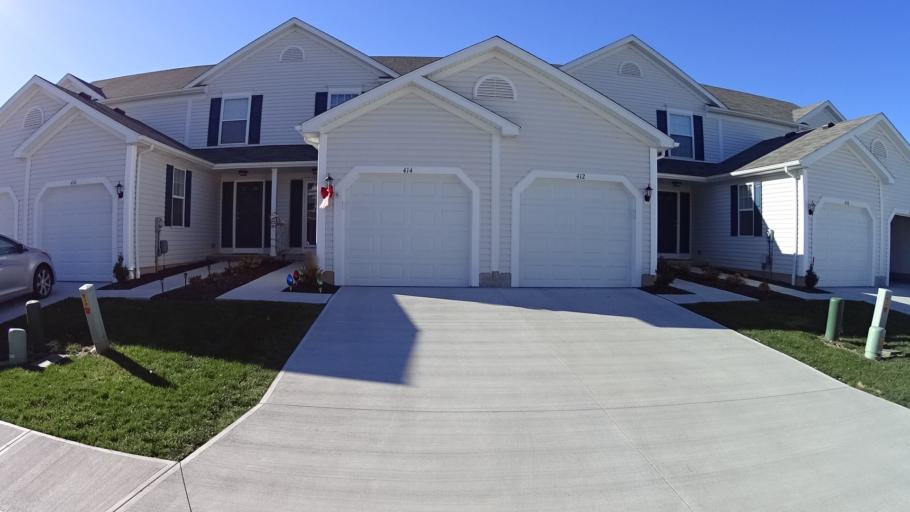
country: US
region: Ohio
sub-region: Lorain County
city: Avon Lake
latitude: 41.4953
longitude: -82.0489
